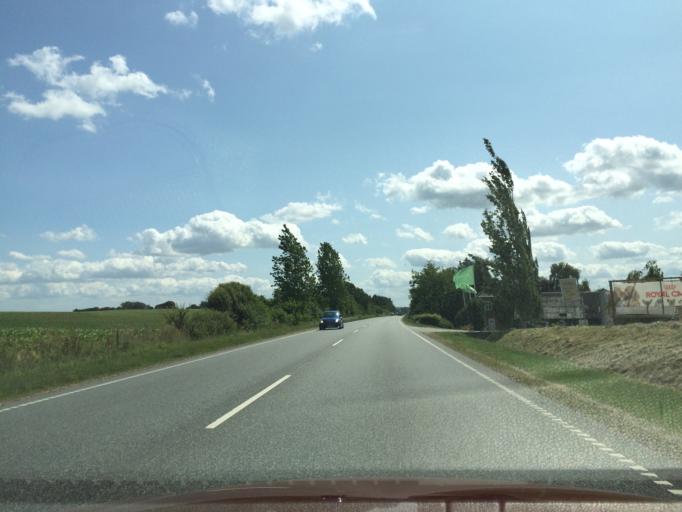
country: DK
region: Central Jutland
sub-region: Favrskov Kommune
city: Hammel
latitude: 56.2538
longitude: 9.7631
